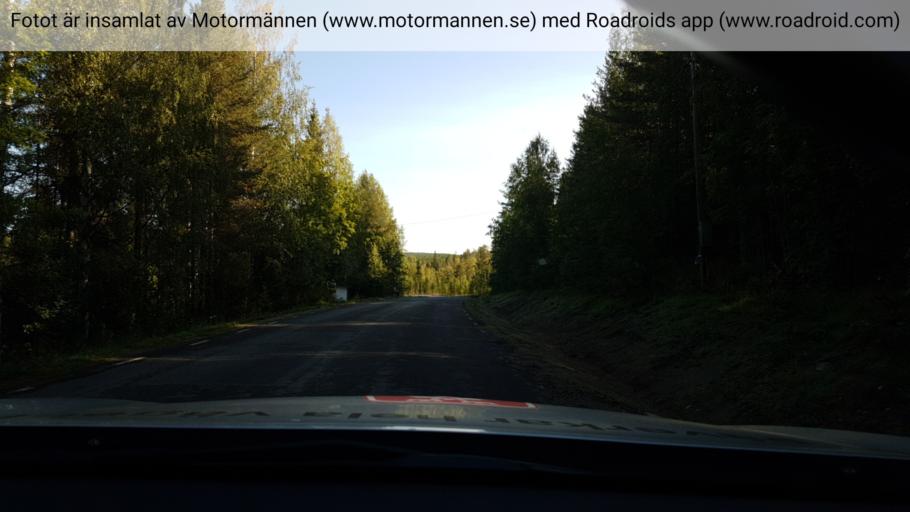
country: SE
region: Vaesterbotten
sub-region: Lycksele Kommun
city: Lycksele
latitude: 64.4177
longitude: 18.8277
